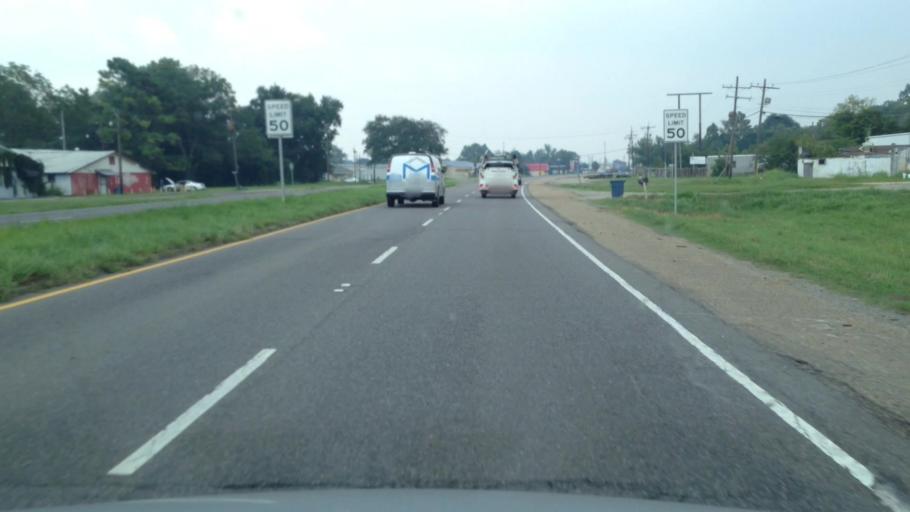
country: US
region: Louisiana
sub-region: West Baton Rouge Parish
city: Port Allen
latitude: 30.5045
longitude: -91.2293
